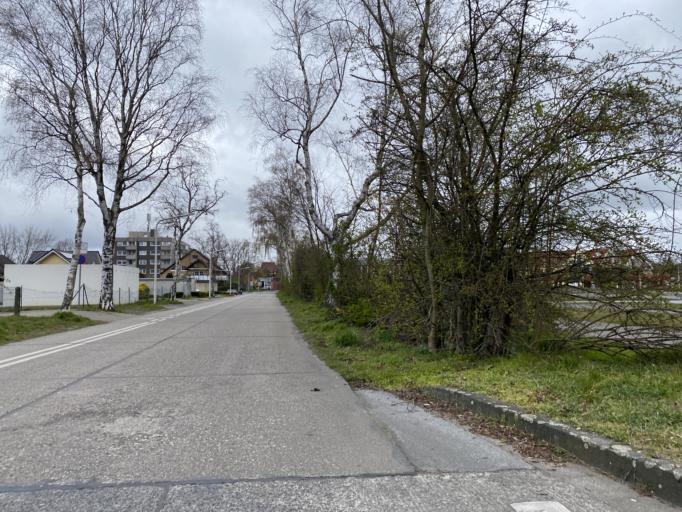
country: DE
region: North Rhine-Westphalia
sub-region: Regierungsbezirk Arnsberg
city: Hamm
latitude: 51.6872
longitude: 7.8834
